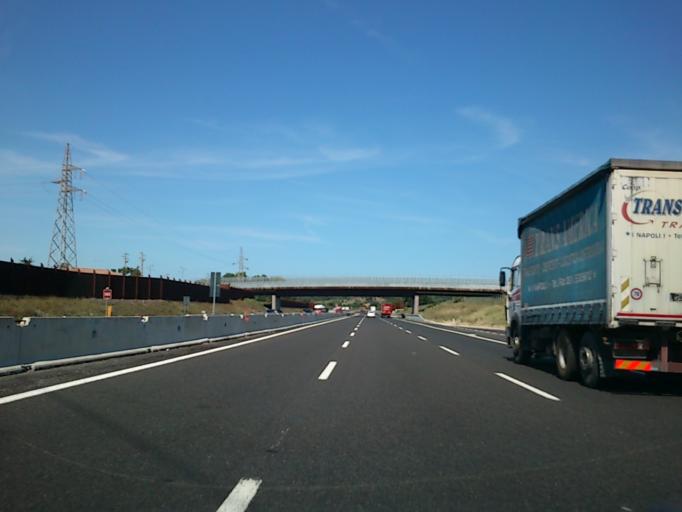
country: IT
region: The Marches
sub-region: Provincia di Pesaro e Urbino
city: Centinarola
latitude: 43.8294
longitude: 12.9959
